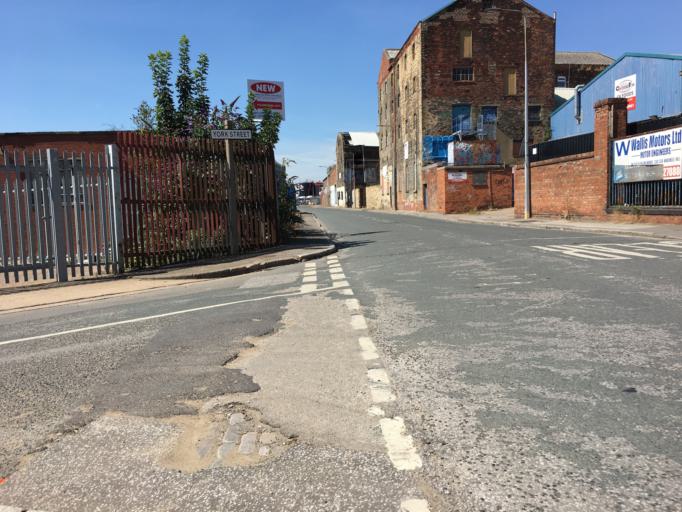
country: GB
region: England
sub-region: City of Kingston upon Hull
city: Hull
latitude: 53.7560
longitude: -0.3316
